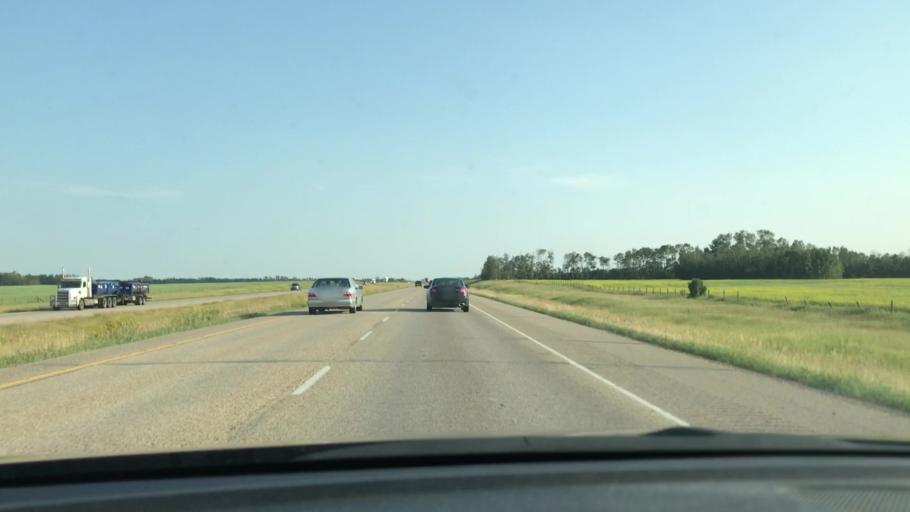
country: CA
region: Alberta
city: Millet
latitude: 53.1305
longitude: -113.5983
